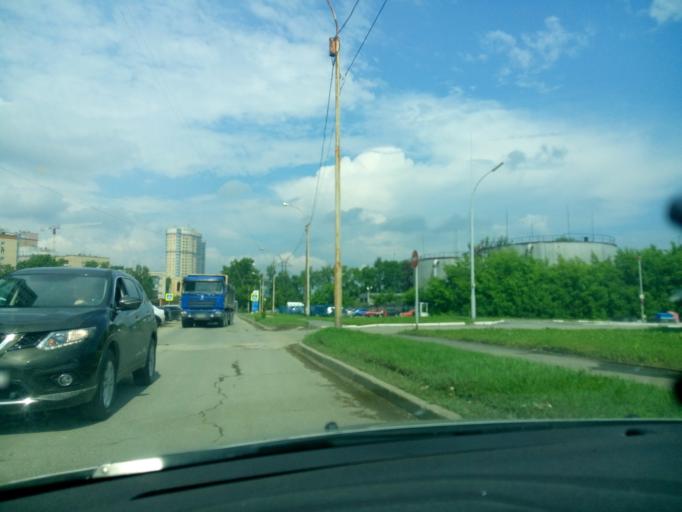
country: RU
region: Sverdlovsk
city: Yekaterinburg
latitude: 56.8594
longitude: 60.6624
